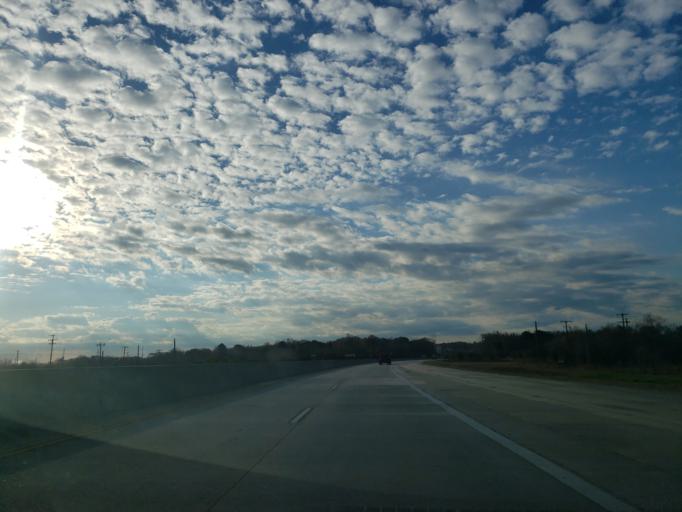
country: US
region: Georgia
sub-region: Chatham County
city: Port Wentworth
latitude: 32.1333
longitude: -81.1647
